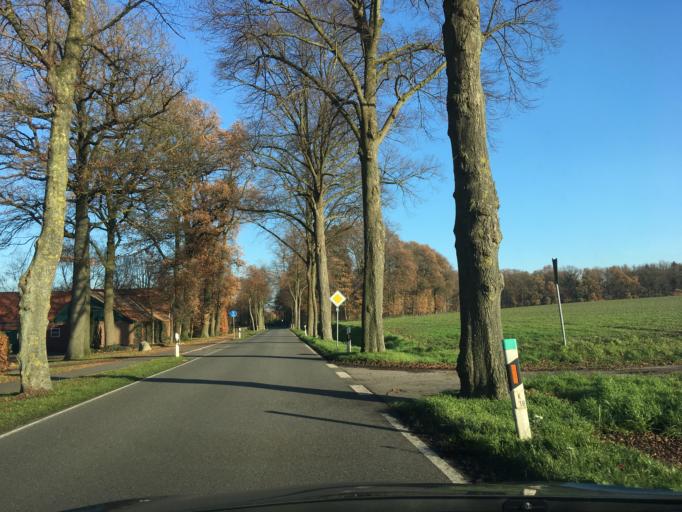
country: DE
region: North Rhine-Westphalia
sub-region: Regierungsbezirk Munster
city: Vreden
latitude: 52.1067
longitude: 6.8727
